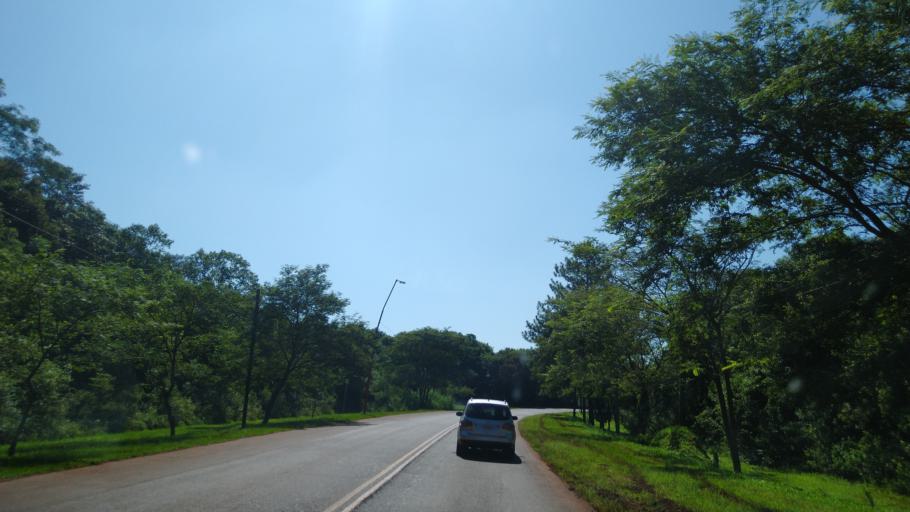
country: AR
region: Misiones
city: Puerto Esperanza
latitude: -26.0194
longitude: -54.5932
